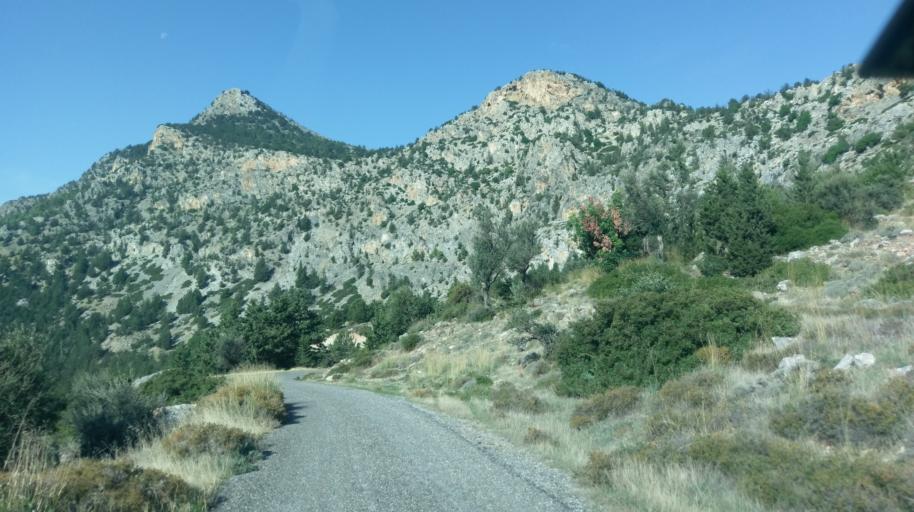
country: CY
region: Keryneia
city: Kyrenia
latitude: 35.2850
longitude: 33.3931
